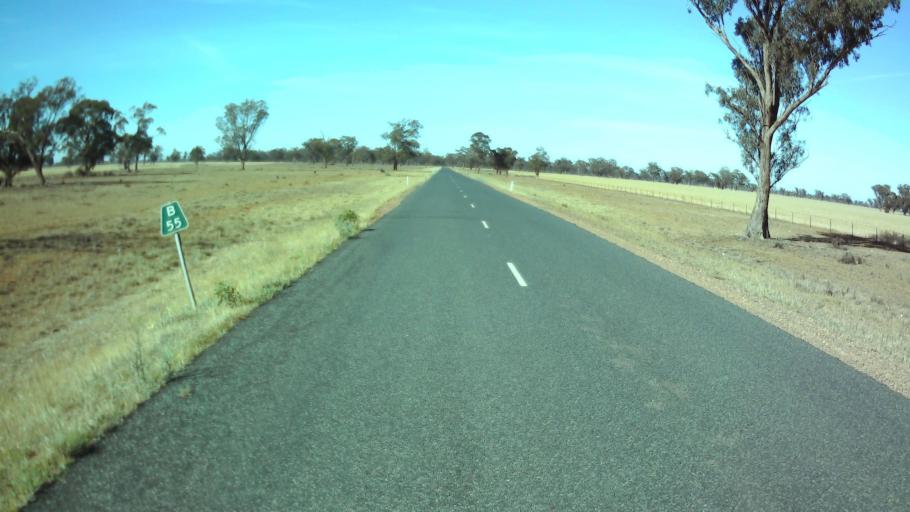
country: AU
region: New South Wales
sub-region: Weddin
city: Grenfell
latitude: -34.0528
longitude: 147.9173
